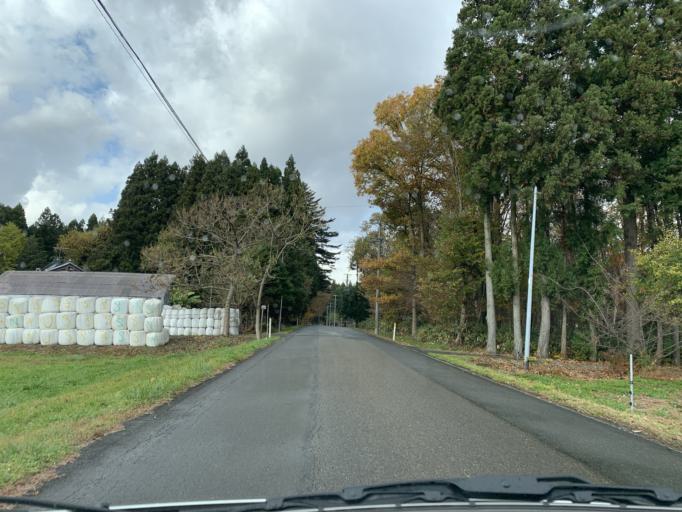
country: JP
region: Iwate
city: Mizusawa
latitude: 39.1013
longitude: 140.9963
